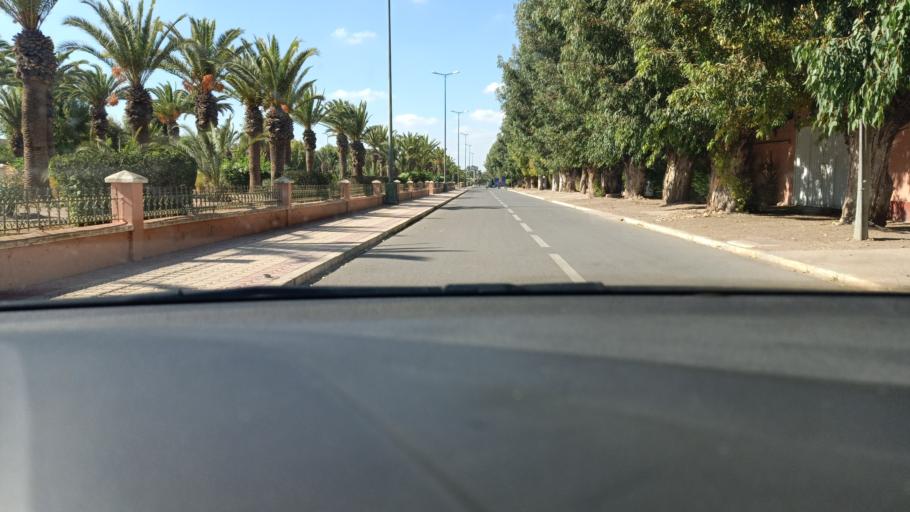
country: MA
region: Doukkala-Abda
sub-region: Safi
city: Youssoufia
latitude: 32.2453
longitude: -8.5298
